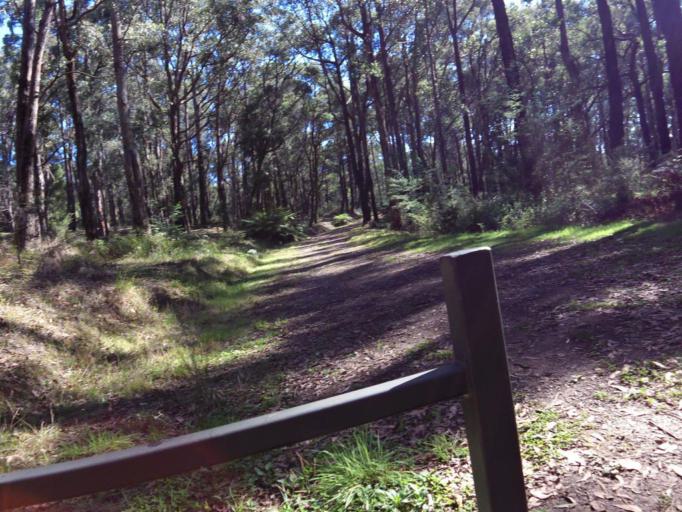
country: AU
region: Victoria
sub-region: Cardinia
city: Cockatoo
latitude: -37.9337
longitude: 145.4714
